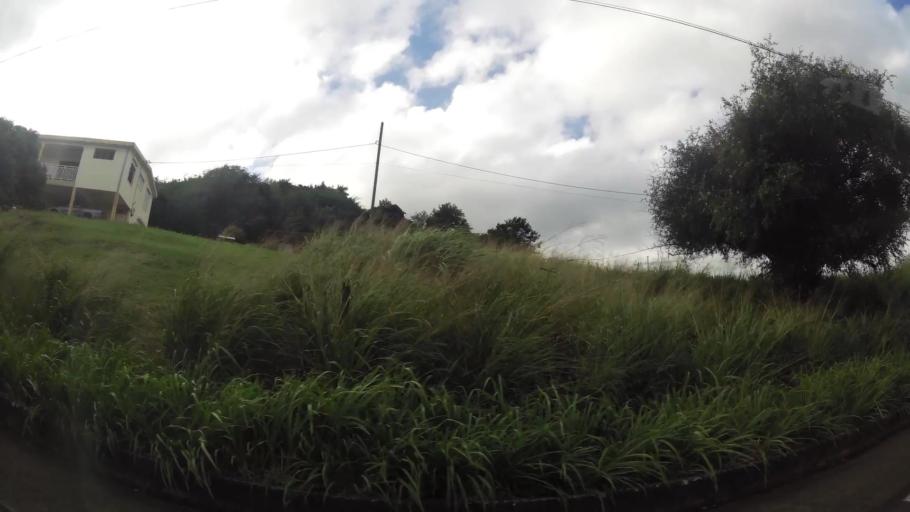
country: MQ
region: Martinique
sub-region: Martinique
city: Le Vauclin
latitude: 14.5809
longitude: -60.8700
